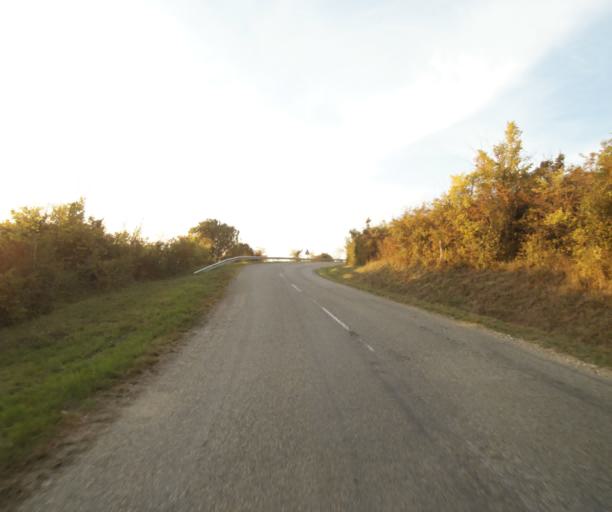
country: FR
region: Midi-Pyrenees
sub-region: Departement du Tarn-et-Garonne
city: Grisolles
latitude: 43.8319
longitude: 1.3074
